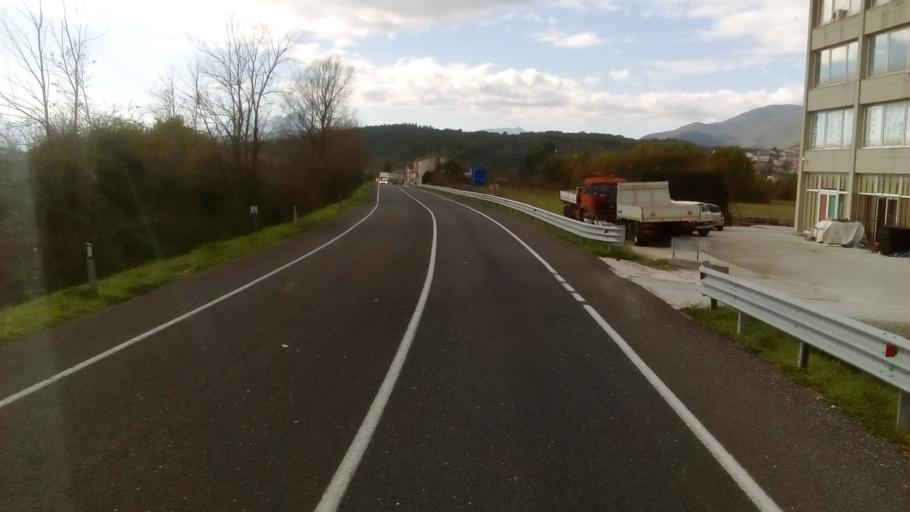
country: IT
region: Molise
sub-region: Provincia di Isernia
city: Macchia d'Isernia
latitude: 41.5615
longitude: 14.1810
